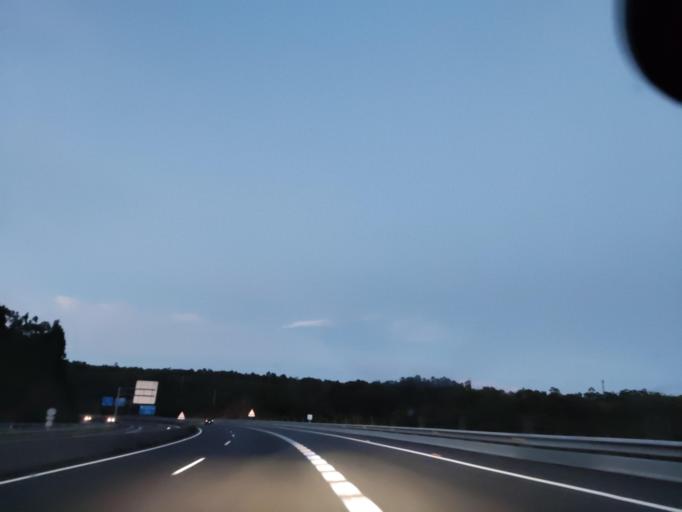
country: ES
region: Galicia
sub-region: Provincia da Coruna
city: Boiro
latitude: 42.6571
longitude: -8.8774
